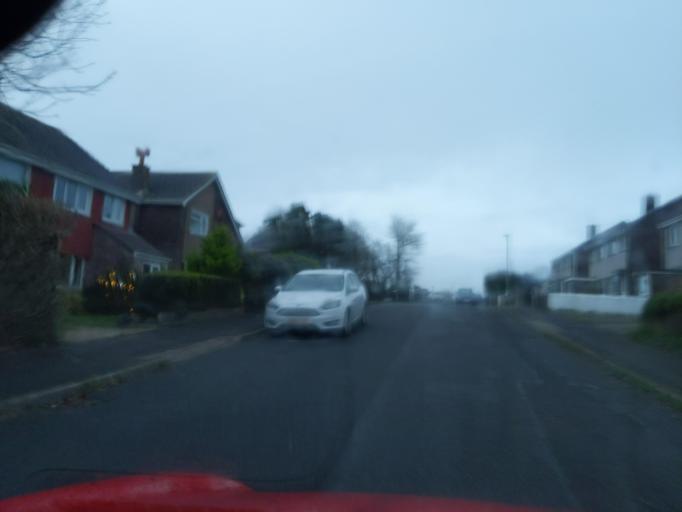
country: GB
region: England
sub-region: Devon
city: Wembury
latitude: 50.3264
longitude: -4.0707
